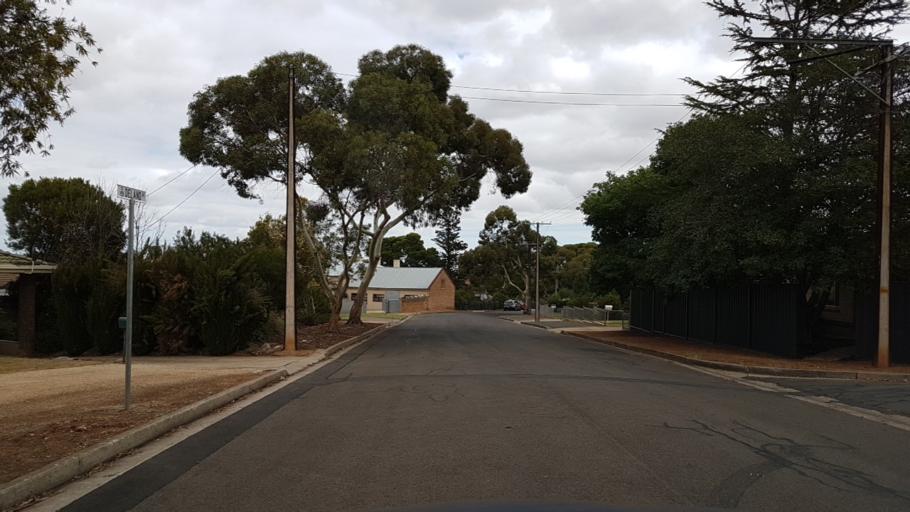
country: AU
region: South Australia
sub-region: Gawler
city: Gawler
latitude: -34.6040
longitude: 138.7596
